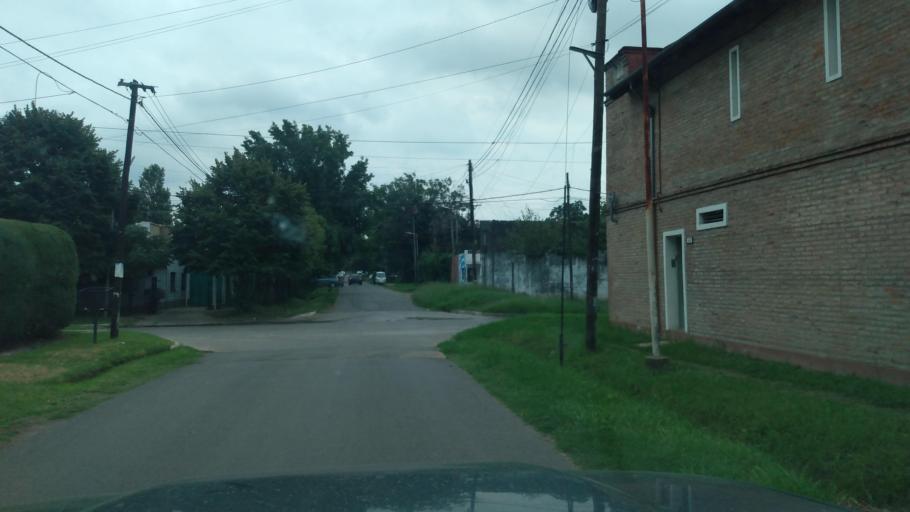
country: AR
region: Buenos Aires
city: Hurlingham
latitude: -34.5716
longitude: -58.6960
